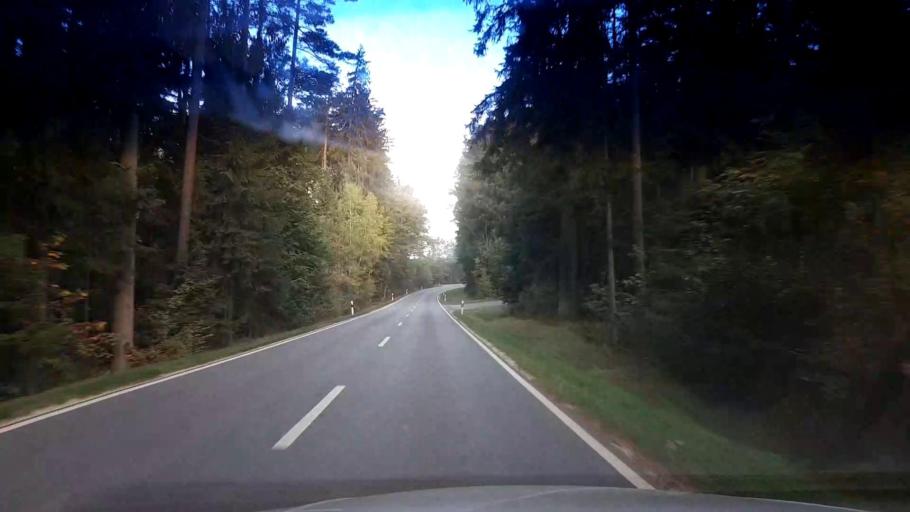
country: DE
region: Bavaria
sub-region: Upper Franconia
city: Weismain
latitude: 50.1008
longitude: 11.2534
